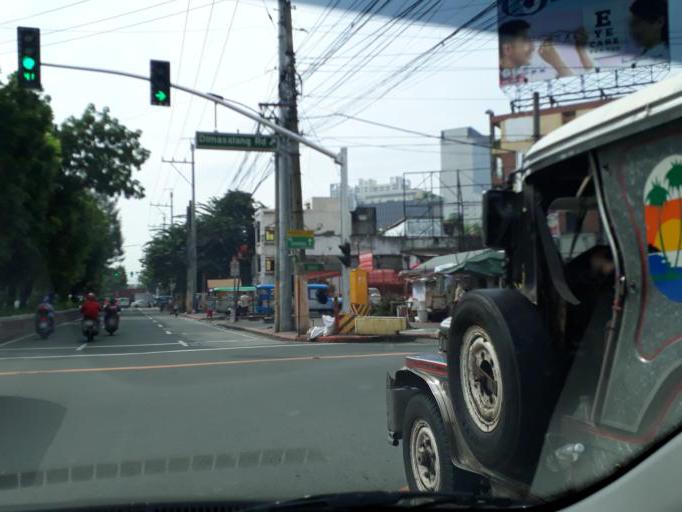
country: PH
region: Metro Manila
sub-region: City of Manila
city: Manila
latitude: 14.6141
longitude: 120.9884
